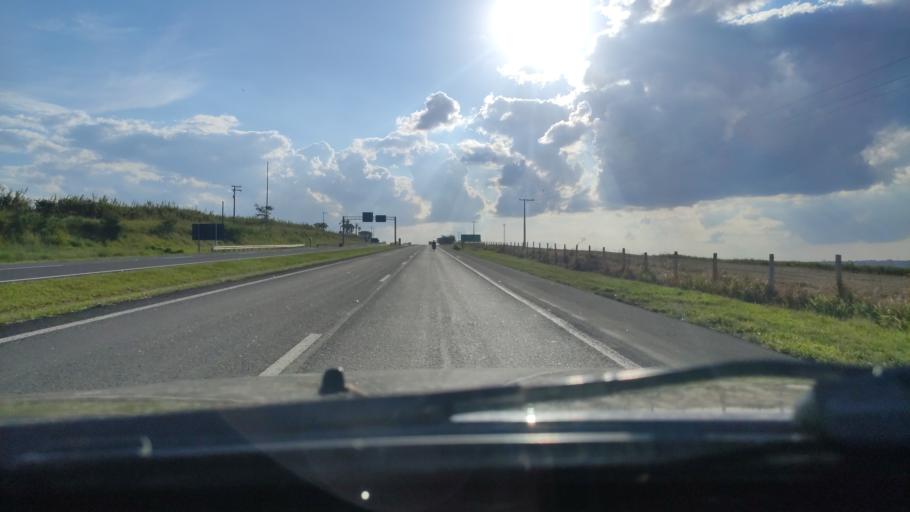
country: BR
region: Sao Paulo
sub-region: Mogi-Mirim
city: Mogi Mirim
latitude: -22.4564
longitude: -46.9097
